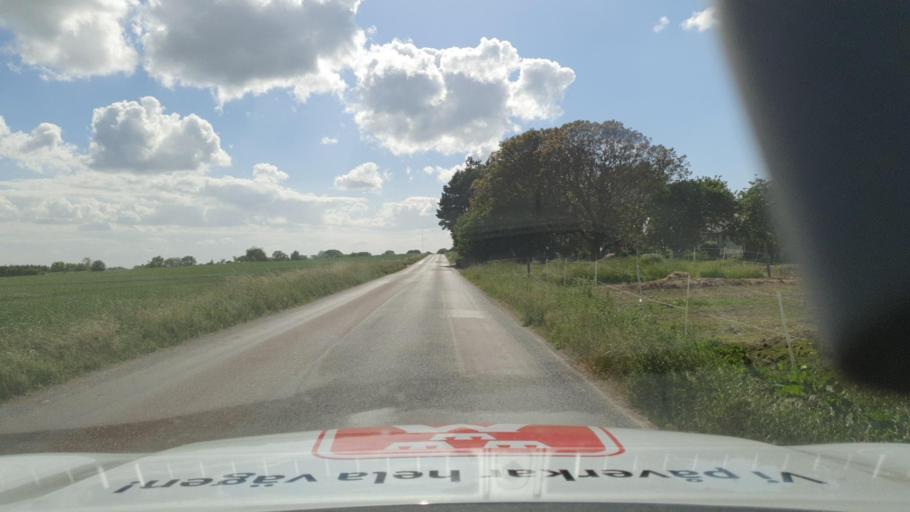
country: SE
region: Skane
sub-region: Simrishamns Kommun
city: Simrishamn
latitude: 55.5636
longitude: 14.3011
